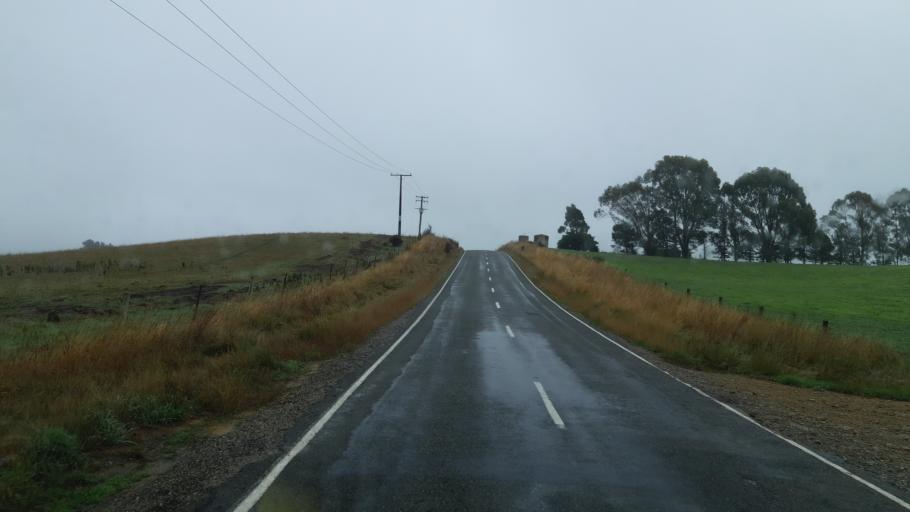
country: NZ
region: Otago
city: Oamaru
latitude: -44.9376
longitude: 170.7650
